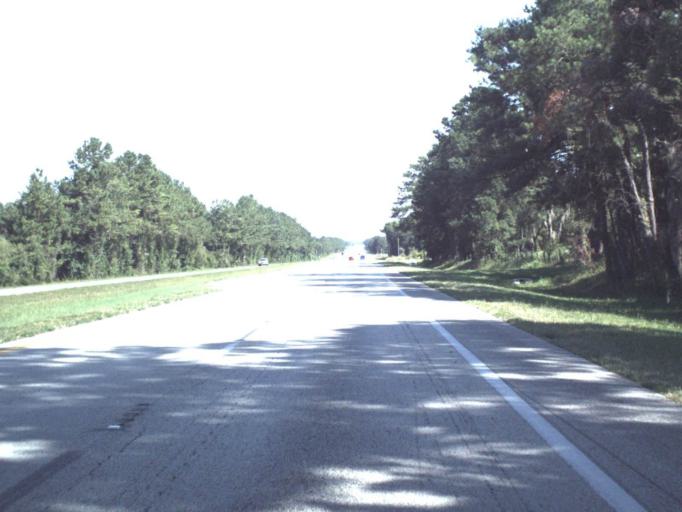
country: US
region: Florida
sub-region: Alachua County
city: Hawthorne
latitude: 29.6680
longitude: -82.1183
